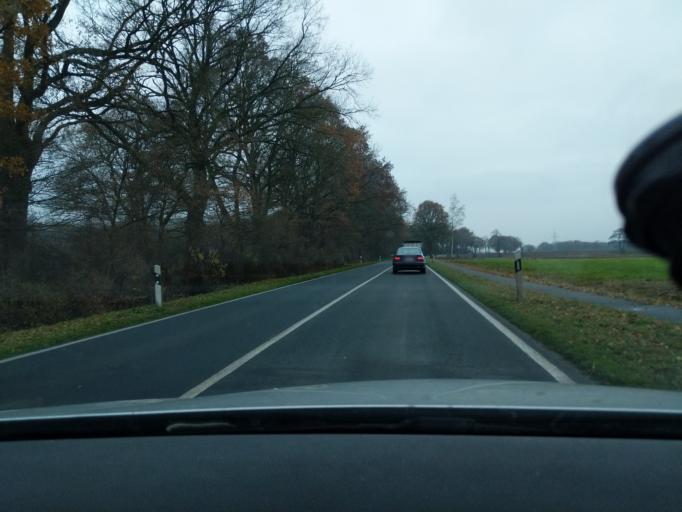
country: DE
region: Lower Saxony
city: Heeslingen
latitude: 53.3088
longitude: 9.3250
